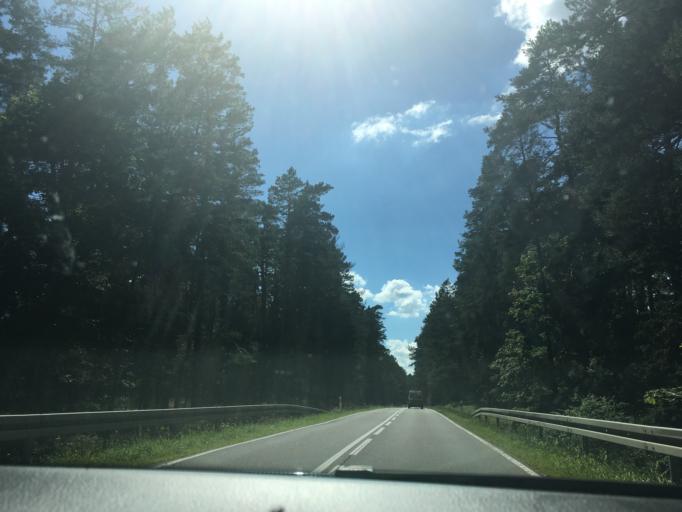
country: PL
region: Podlasie
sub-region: Powiat augustowski
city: Augustow
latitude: 53.8591
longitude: 23.0822
